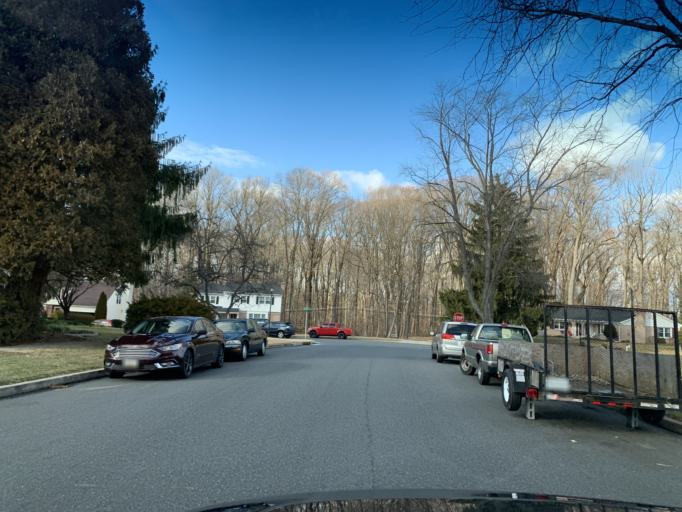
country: US
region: Maryland
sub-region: Harford County
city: South Bel Air
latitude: 39.5332
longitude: -76.3373
